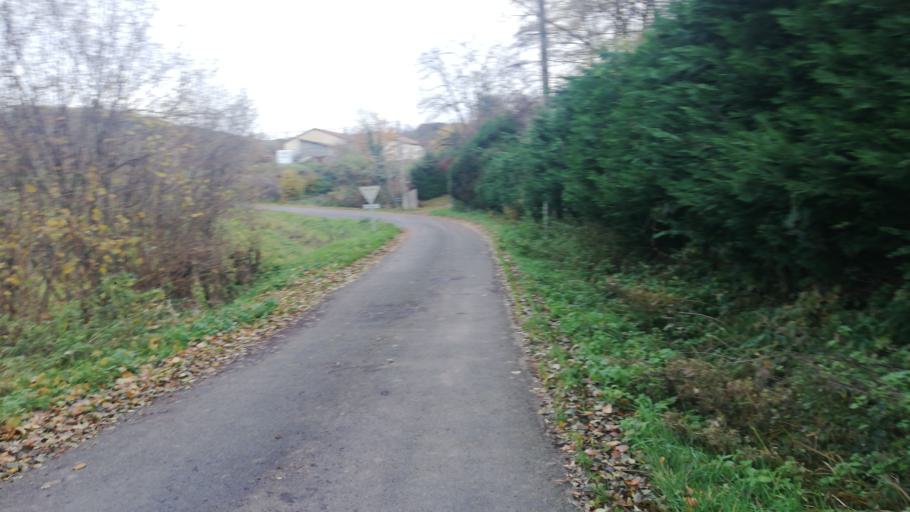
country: FR
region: Auvergne
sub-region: Departement du Puy-de-Dome
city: Billom
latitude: 45.6875
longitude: 3.3697
